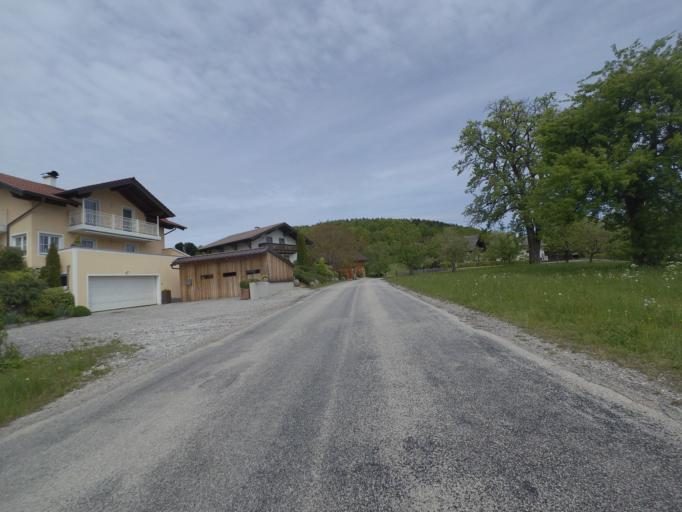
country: AT
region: Salzburg
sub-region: Politischer Bezirk Salzburg-Umgebung
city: Schleedorf
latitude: 47.9945
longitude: 13.1393
